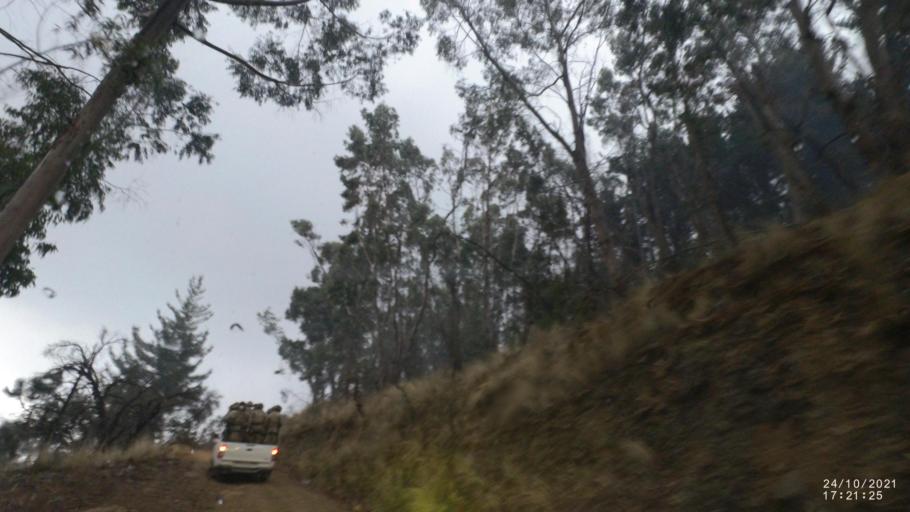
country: BO
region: Cochabamba
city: Cochabamba
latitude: -17.3274
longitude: -66.1345
